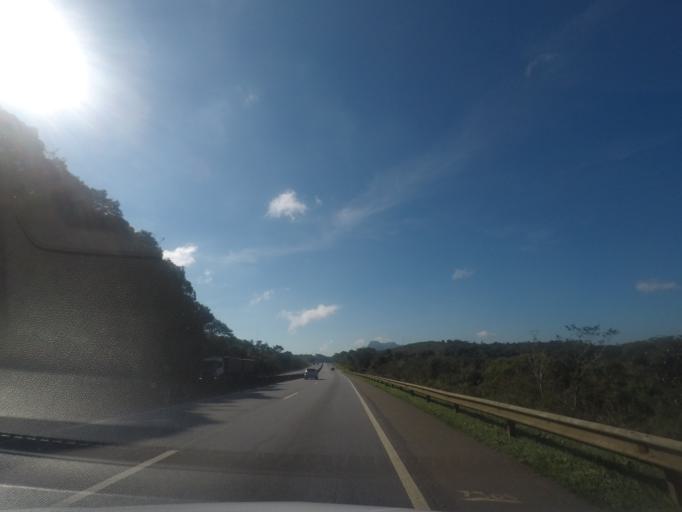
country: BR
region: Parana
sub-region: Piraquara
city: Piraquara
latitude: -25.5884
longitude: -48.9457
